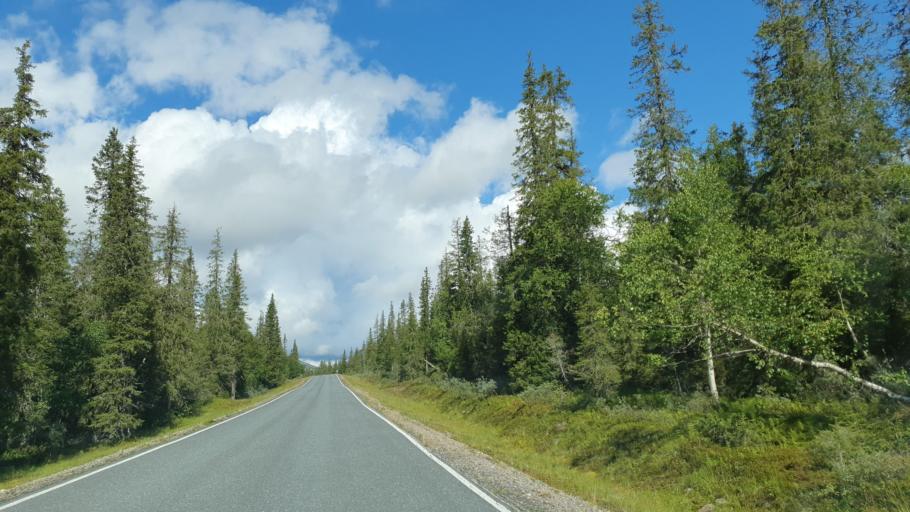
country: FI
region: Lapland
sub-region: Tunturi-Lappi
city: Muonio
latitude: 68.0389
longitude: 24.0664
